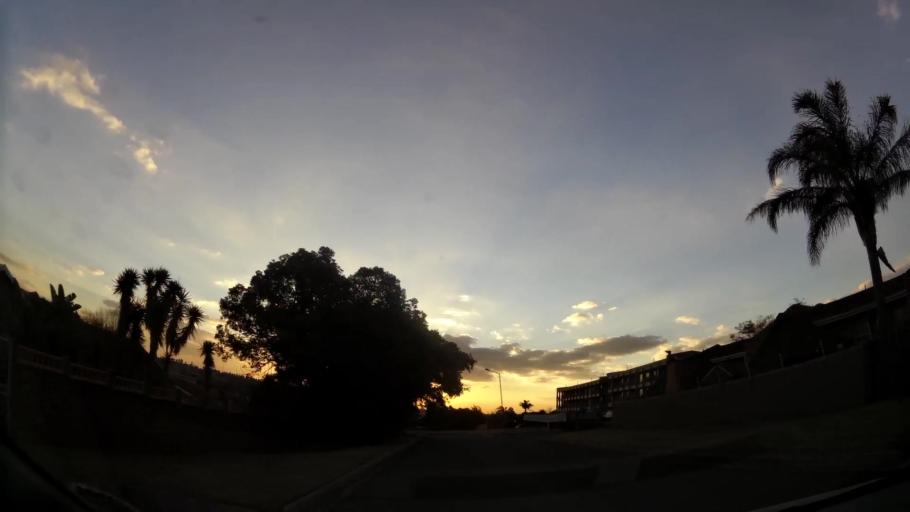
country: ZA
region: Gauteng
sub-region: West Rand District Municipality
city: Krugersdorp
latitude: -26.0732
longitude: 27.7836
